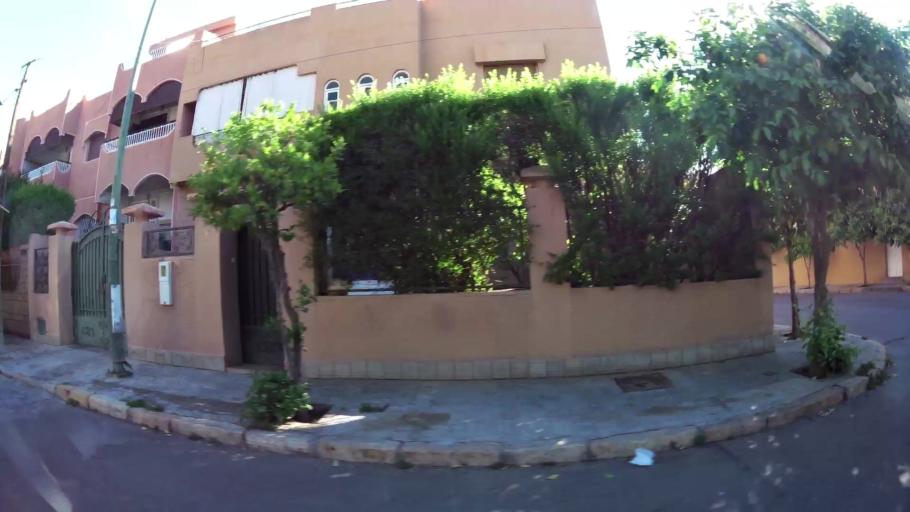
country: MA
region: Marrakech-Tensift-Al Haouz
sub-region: Marrakech
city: Marrakesh
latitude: 31.6447
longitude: -8.0135
